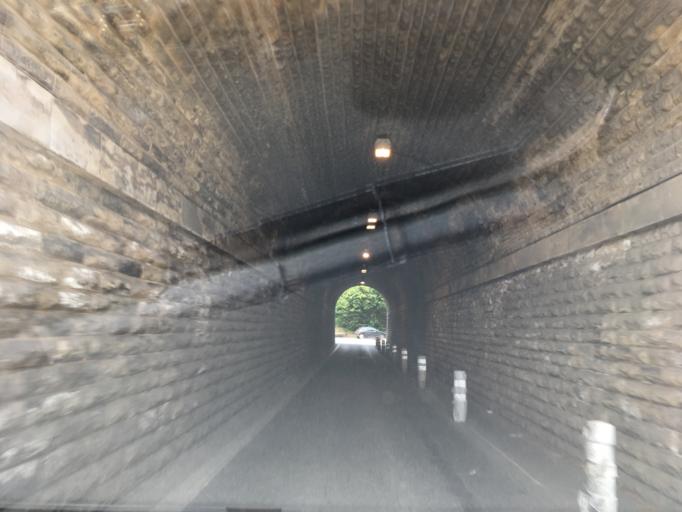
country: FR
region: Poitou-Charentes
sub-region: Departement des Deux-Sevres
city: Niort
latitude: 46.3140
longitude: -0.4582
